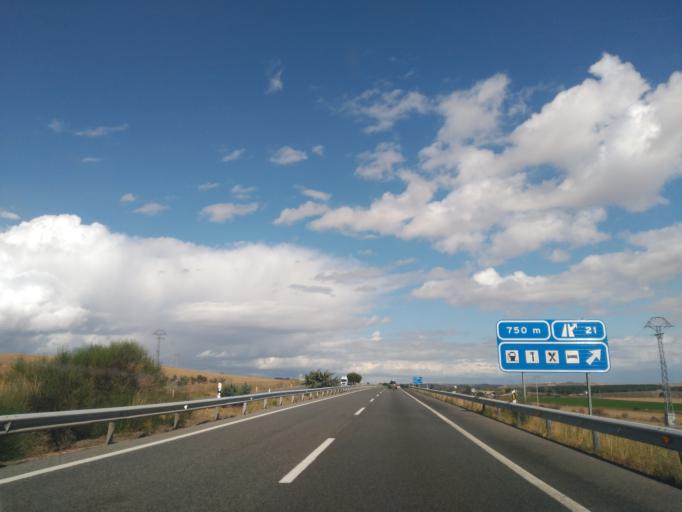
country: ES
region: Castille and Leon
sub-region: Provincia de Burgos
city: Estepar
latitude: 42.2713
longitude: -3.9098
